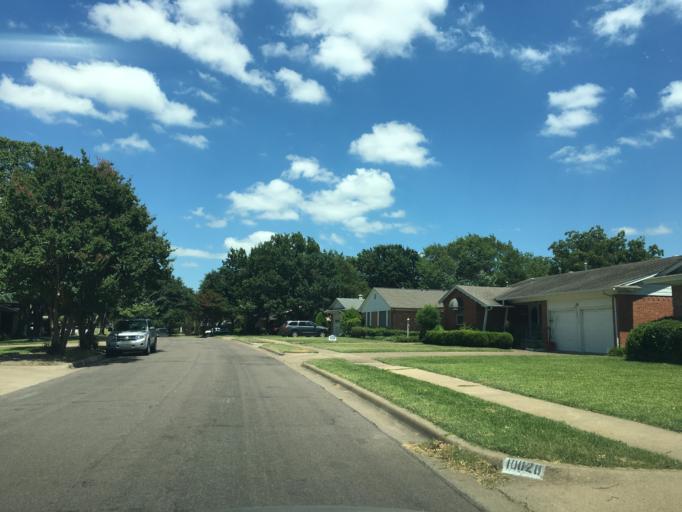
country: US
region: Texas
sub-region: Dallas County
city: Garland
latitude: 32.8491
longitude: -96.6919
